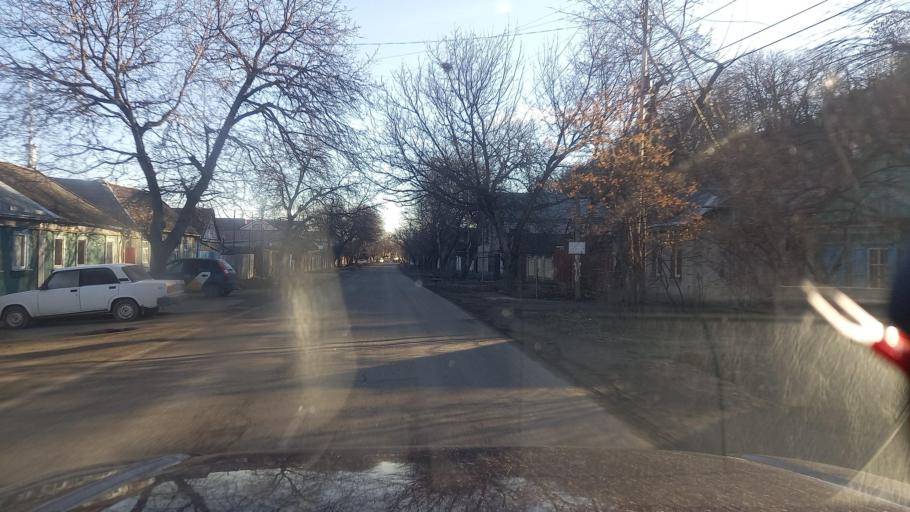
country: RU
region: Stavropol'skiy
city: Svobody
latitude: 44.0237
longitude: 43.0554
